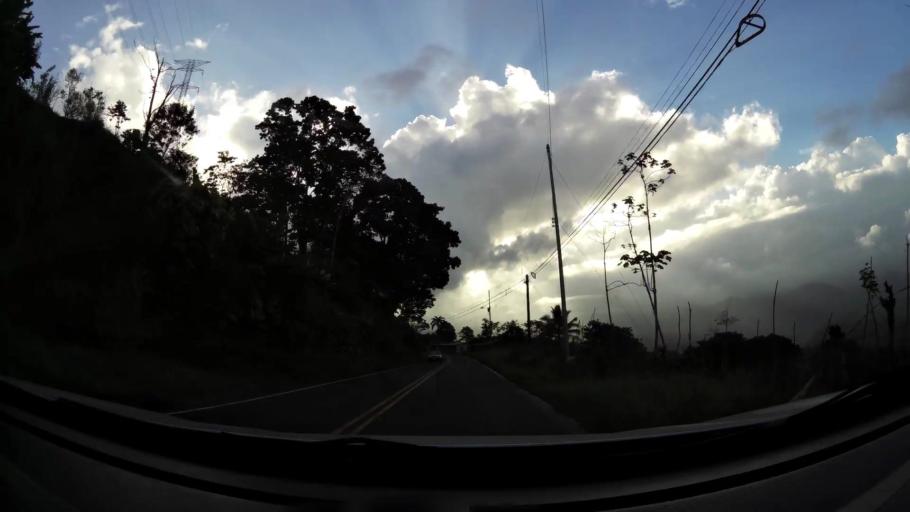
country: CR
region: Limon
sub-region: Canton de Siquirres
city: Siquirres
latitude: 10.0046
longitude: -83.5722
